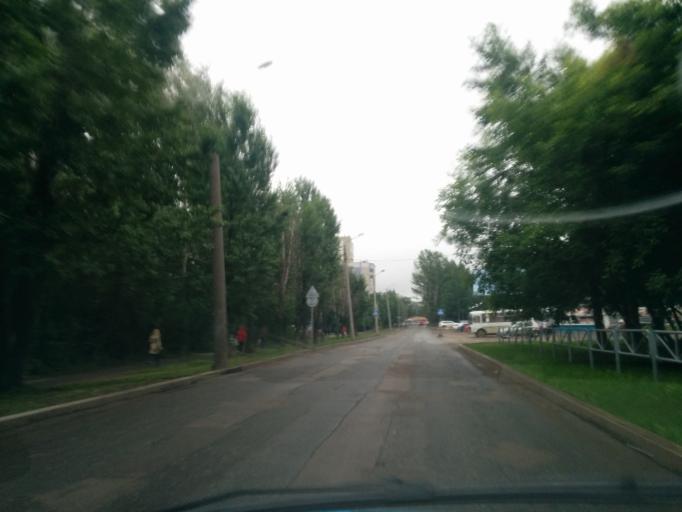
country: RU
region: Perm
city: Perm
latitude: 57.9921
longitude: 56.2311
